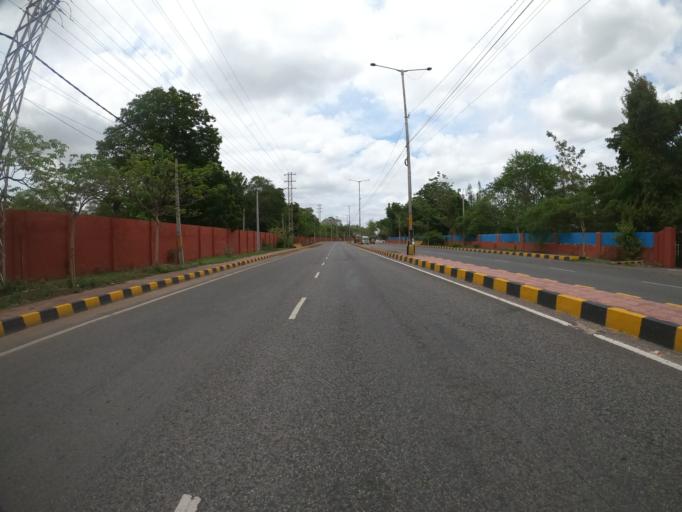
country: IN
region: Telangana
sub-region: Hyderabad
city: Hyderabad
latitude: 17.3764
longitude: 78.3901
